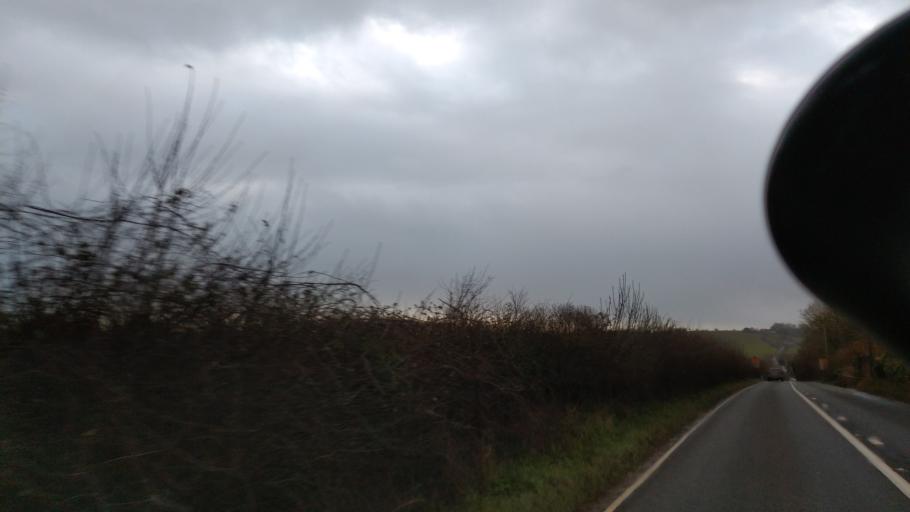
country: GB
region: England
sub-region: Somerset
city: Shepton Mallet
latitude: 51.1572
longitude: -2.5423
